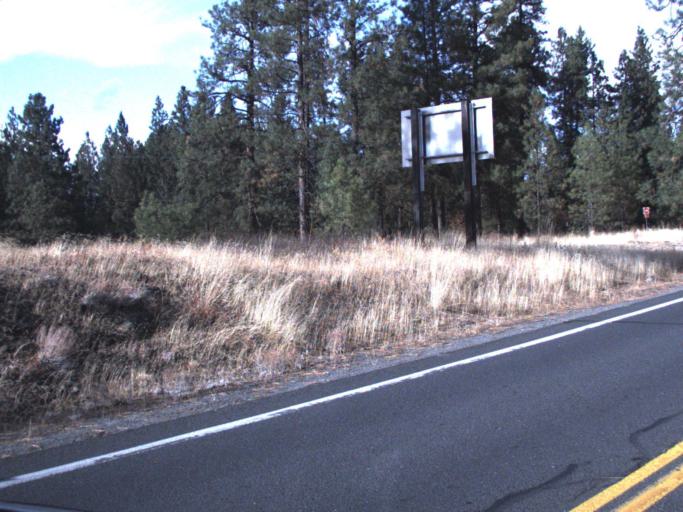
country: US
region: Washington
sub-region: Spokane County
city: Medical Lake
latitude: 47.5611
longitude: -117.6951
